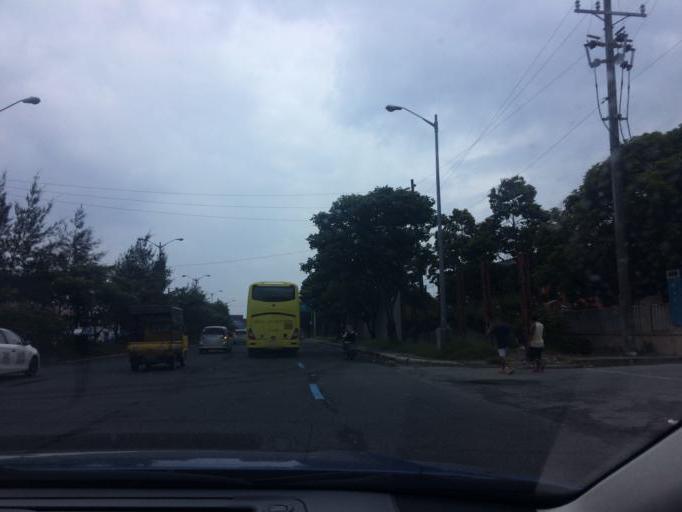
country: PH
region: Metro Manila
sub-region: City of Manila
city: Port Area
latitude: 14.5493
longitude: 120.9866
